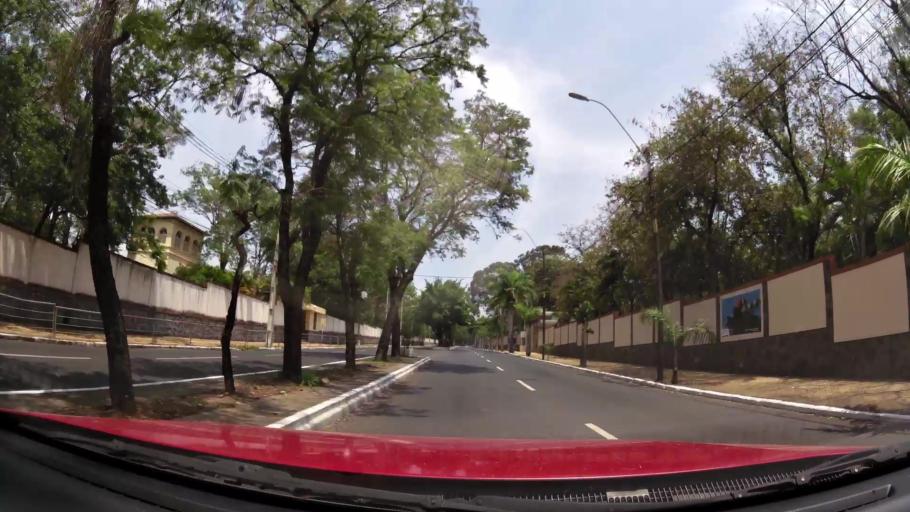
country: PY
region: Asuncion
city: Asuncion
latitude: -25.2953
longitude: -57.6040
